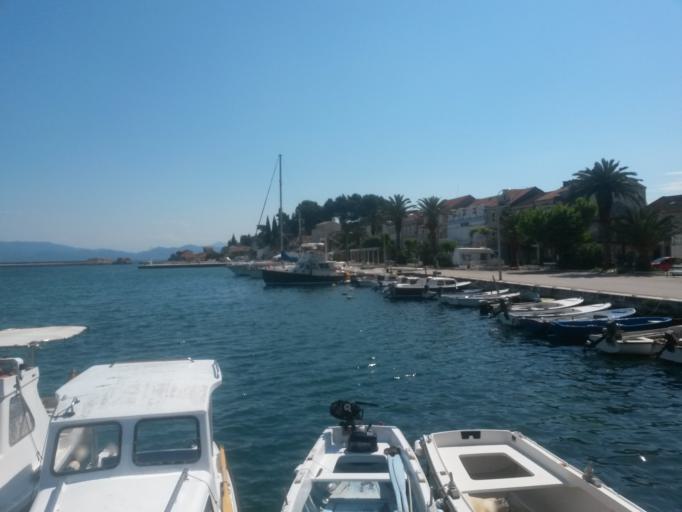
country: HR
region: Dubrovacko-Neretvanska
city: Orebic
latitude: 43.0091
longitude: 17.2654
